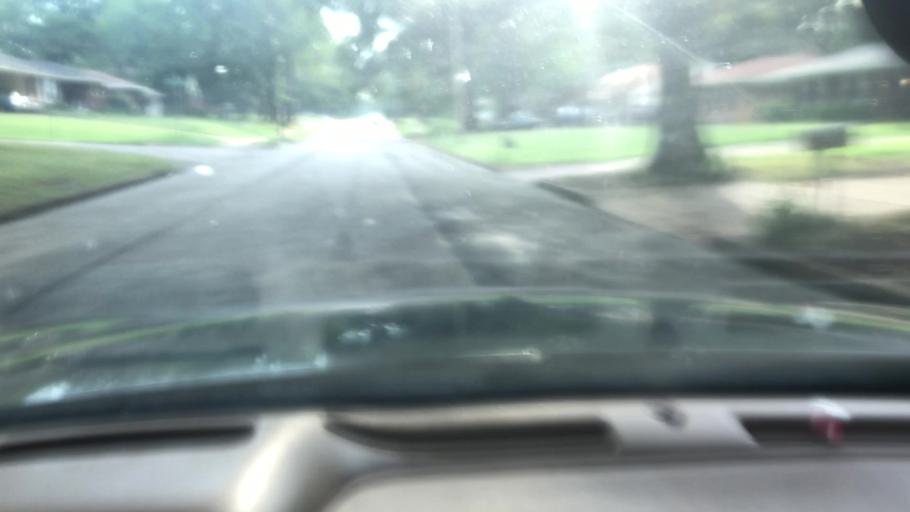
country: US
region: Mississippi
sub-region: De Soto County
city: Southaven
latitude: 35.0466
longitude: -90.0132
